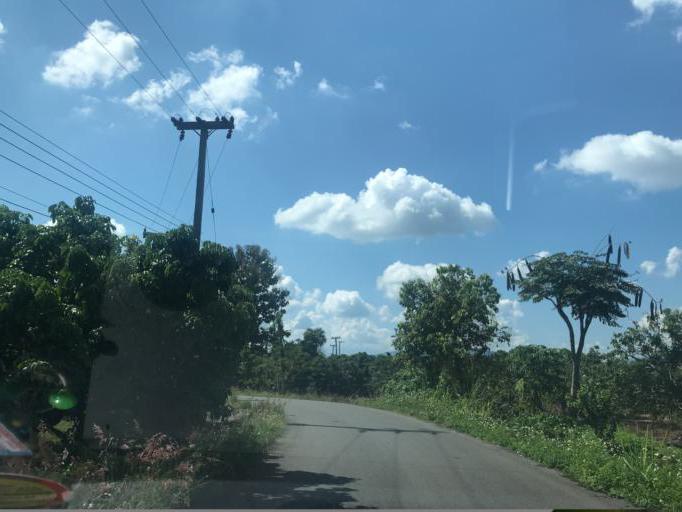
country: TH
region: Chiang Mai
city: Mae Wang
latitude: 18.5653
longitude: 98.8370
